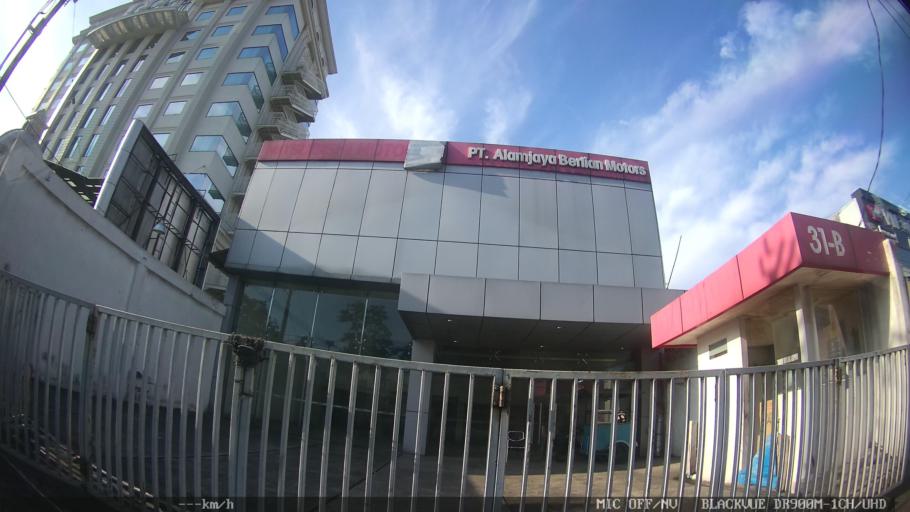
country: ID
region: North Sumatra
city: Medan
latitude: 3.5894
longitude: 98.6512
